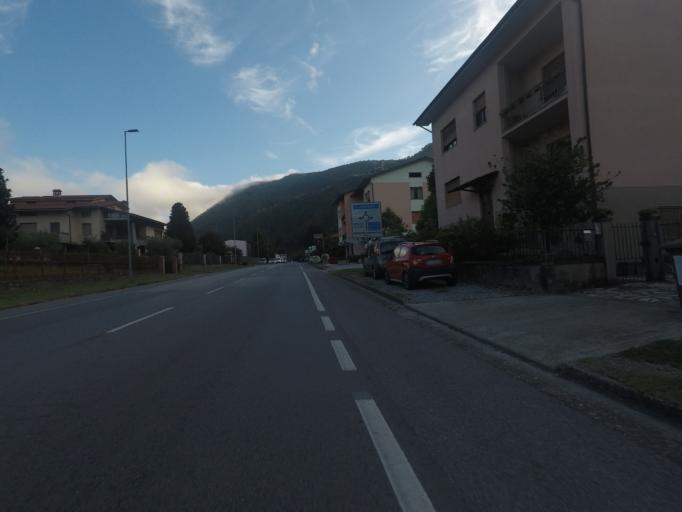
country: IT
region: Tuscany
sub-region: Provincia di Lucca
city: Borgo a Mozzano
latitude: 43.9786
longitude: 10.5486
